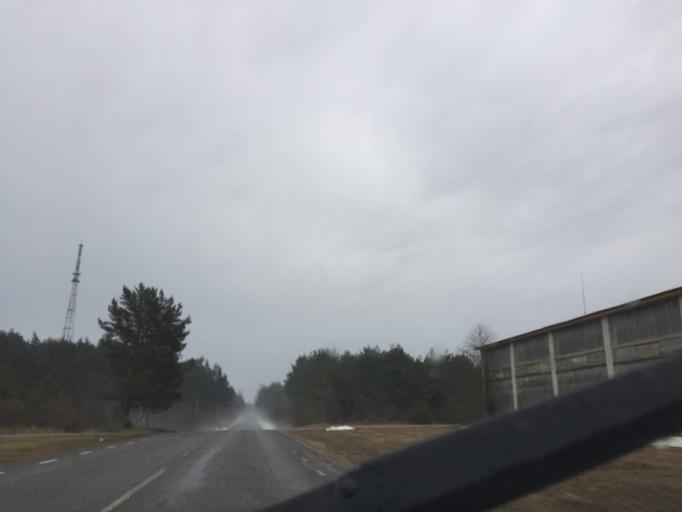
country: EE
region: Saare
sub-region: Orissaare vald
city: Orissaare
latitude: 58.5603
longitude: 23.0547
